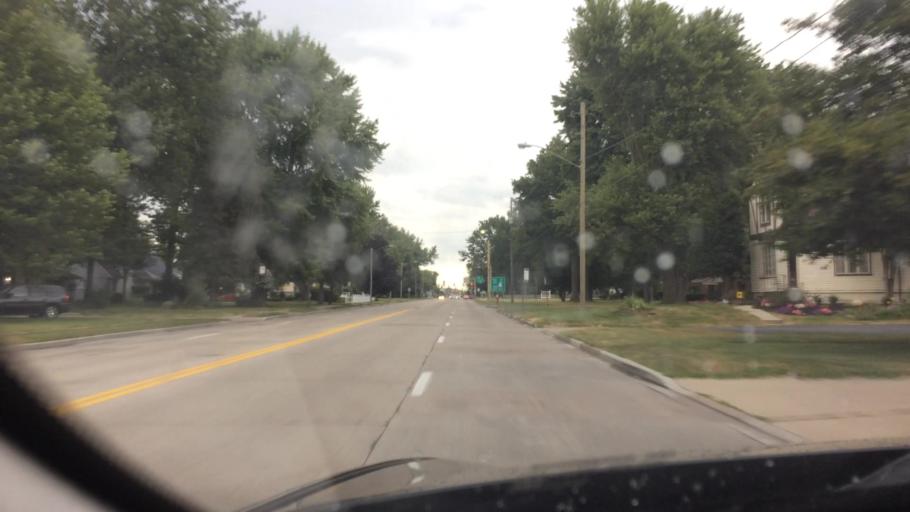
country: US
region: Ohio
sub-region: Lucas County
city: Ottawa Hills
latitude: 41.6844
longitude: -83.6442
